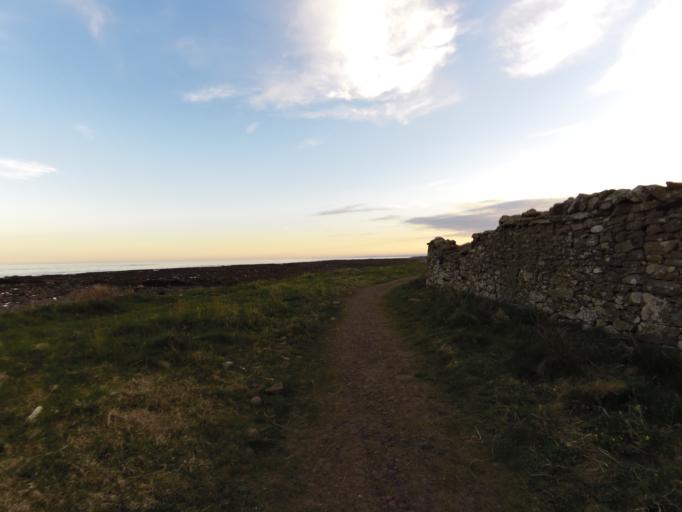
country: GB
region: Scotland
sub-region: Aberdeenshire
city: Inverbervie
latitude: 56.8016
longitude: -2.3165
